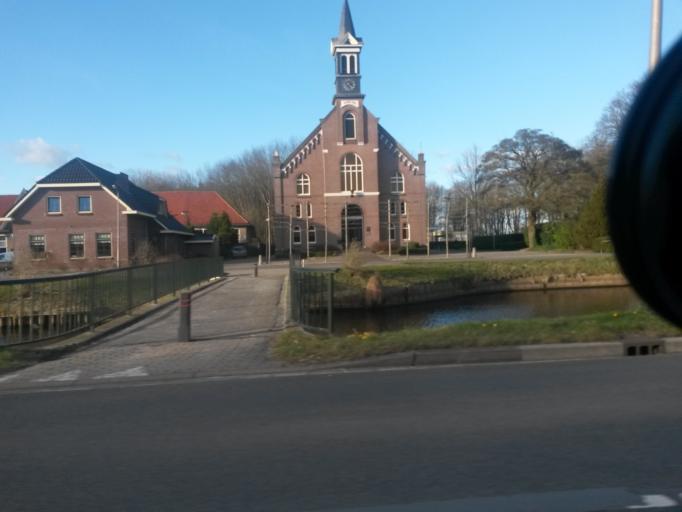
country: NL
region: Overijssel
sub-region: Gemeente Hardenberg
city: Hardenberg
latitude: 52.6517
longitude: 6.6251
